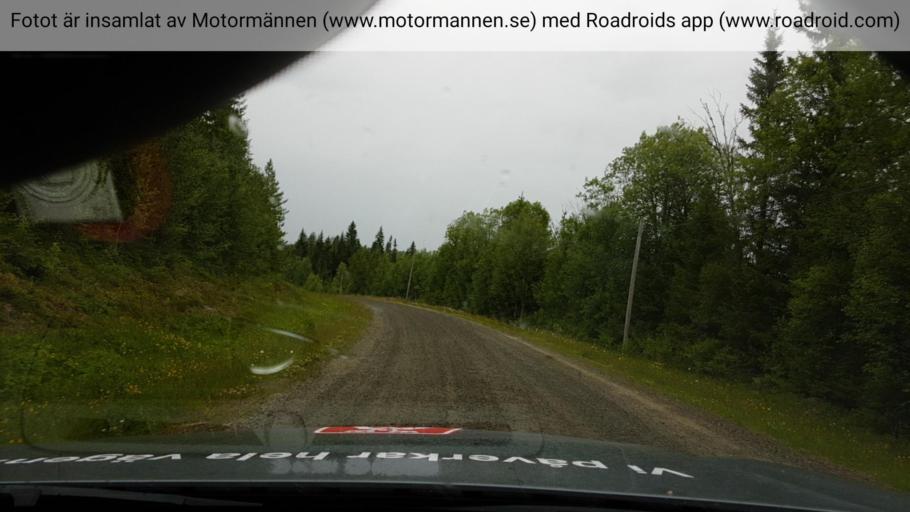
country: SE
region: Jaemtland
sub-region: Bergs Kommun
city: Hoverberg
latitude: 62.5592
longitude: 14.6880
